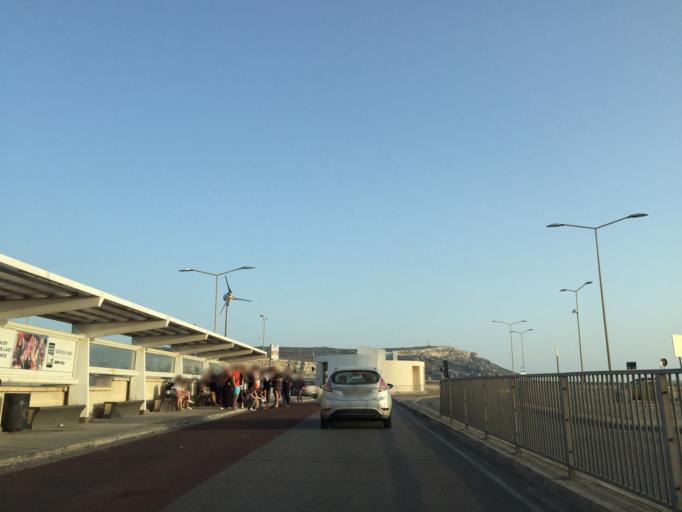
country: MT
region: Il-Mellieha
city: Mellieha
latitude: 35.9877
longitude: 14.3287
